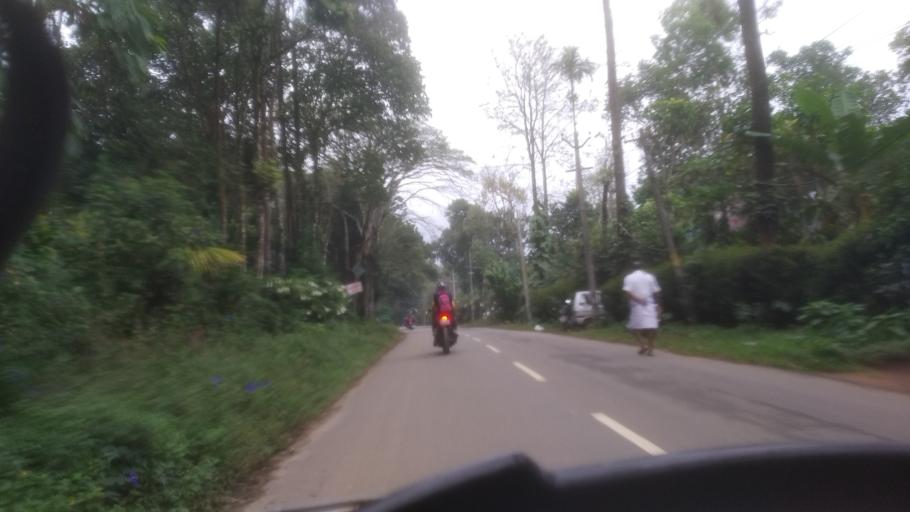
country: IN
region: Tamil Nadu
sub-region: Theni
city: Kombai
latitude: 9.8994
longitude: 77.1820
